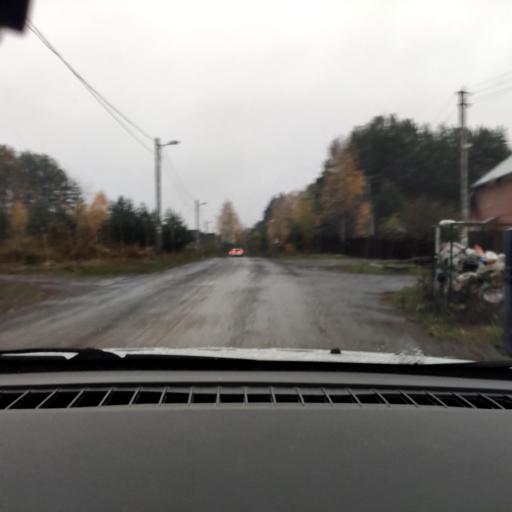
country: RU
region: Perm
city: Kondratovo
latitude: 58.0486
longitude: 56.1031
